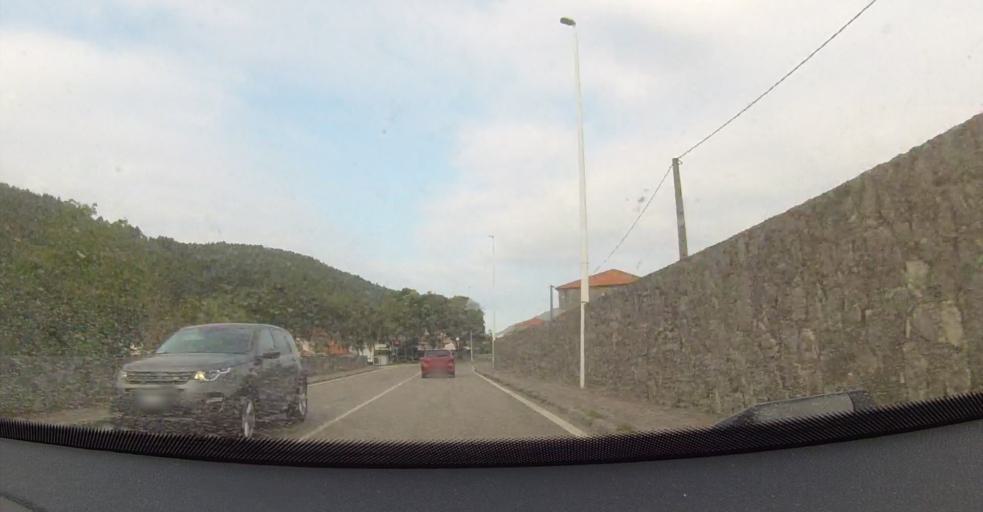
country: ES
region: Cantabria
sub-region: Provincia de Cantabria
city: Argonos
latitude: 43.4569
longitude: -3.4954
